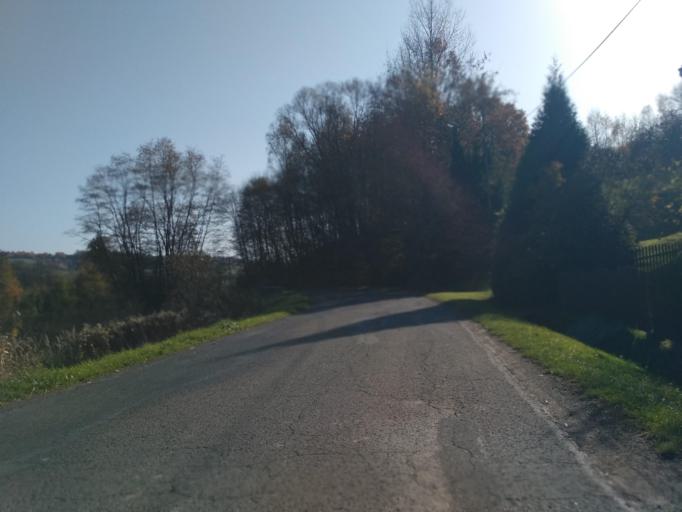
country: PL
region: Subcarpathian Voivodeship
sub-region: Powiat brzozowski
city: Nozdrzec
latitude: 49.7856
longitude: 22.2106
